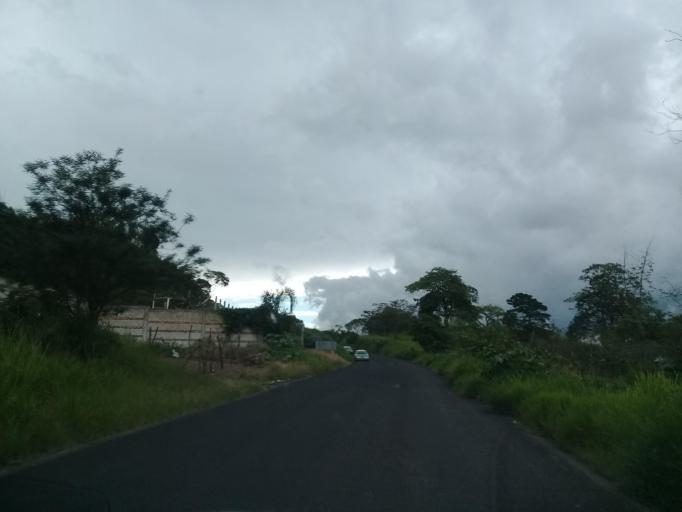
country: MX
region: Veracruz
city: El Castillo
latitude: 19.5584
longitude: -96.8433
